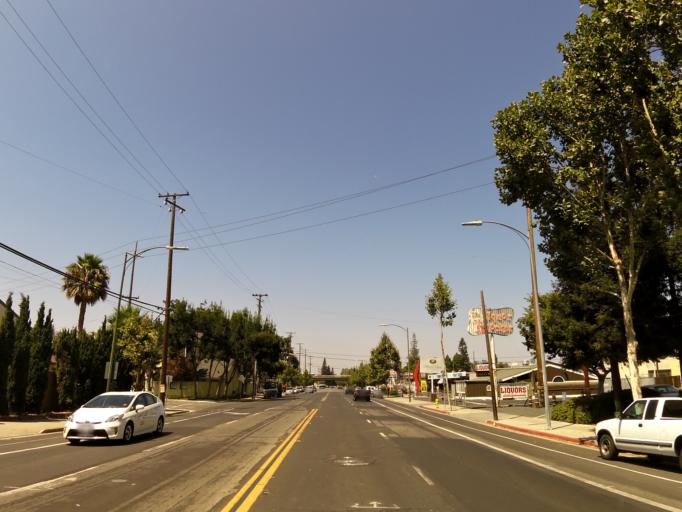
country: US
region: California
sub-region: Santa Clara County
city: Buena Vista
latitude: 37.3138
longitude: -121.9051
